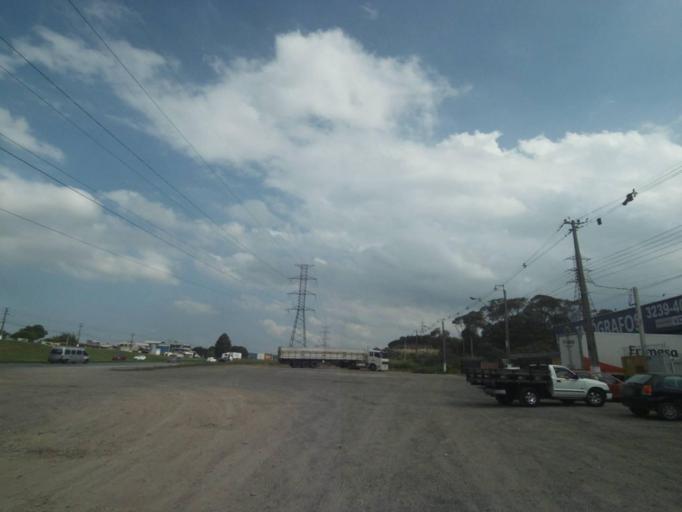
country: BR
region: Parana
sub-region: Curitiba
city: Curitiba
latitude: -25.5057
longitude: -49.3414
